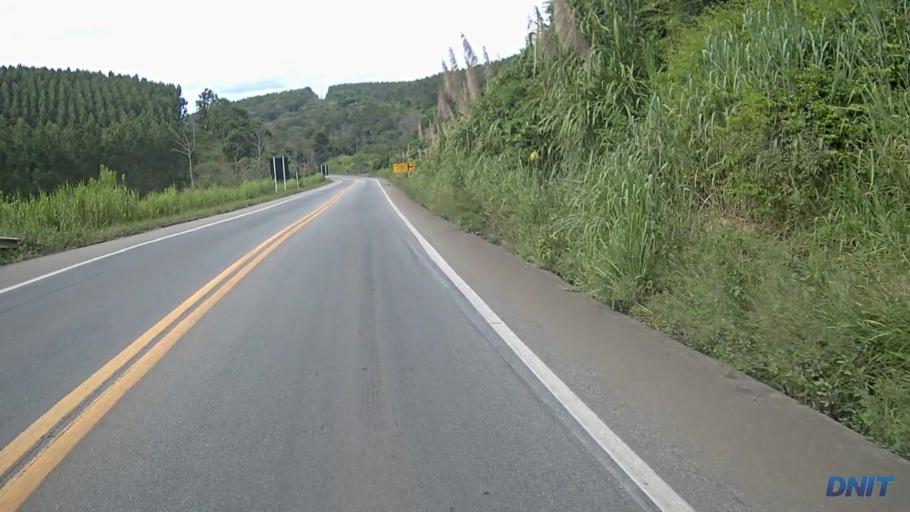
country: BR
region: Minas Gerais
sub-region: Ipaba
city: Ipaba
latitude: -19.3552
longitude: -42.4359
